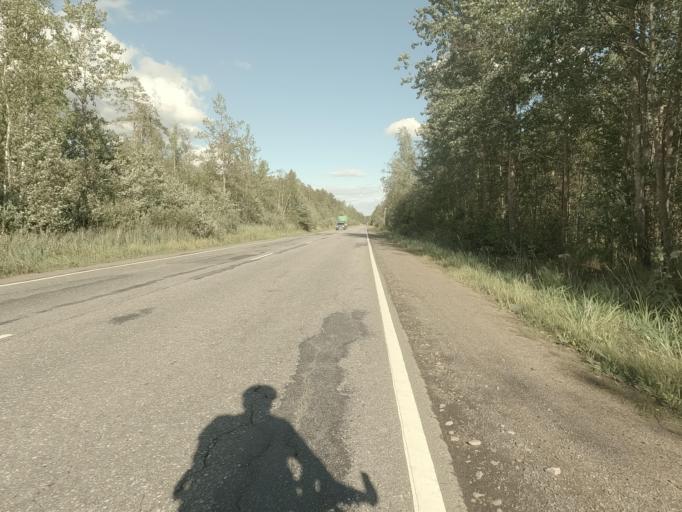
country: RU
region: Leningrad
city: Borisova Griva
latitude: 59.9853
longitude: 30.9087
